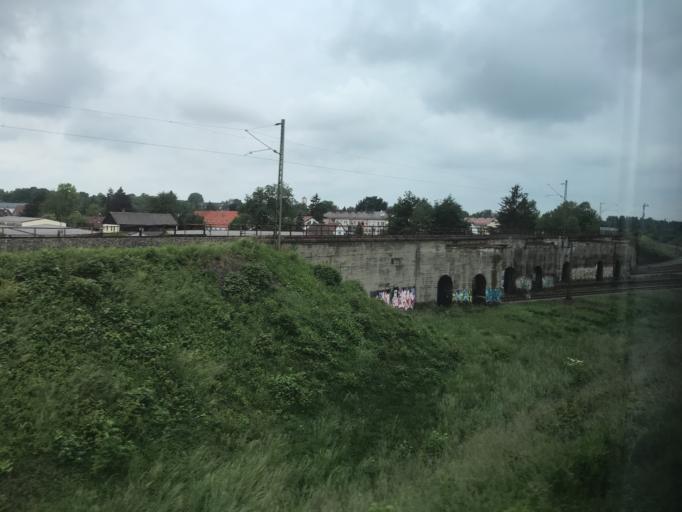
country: DE
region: Bavaria
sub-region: Swabia
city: Gersthofen
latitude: 48.3932
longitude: 10.8698
